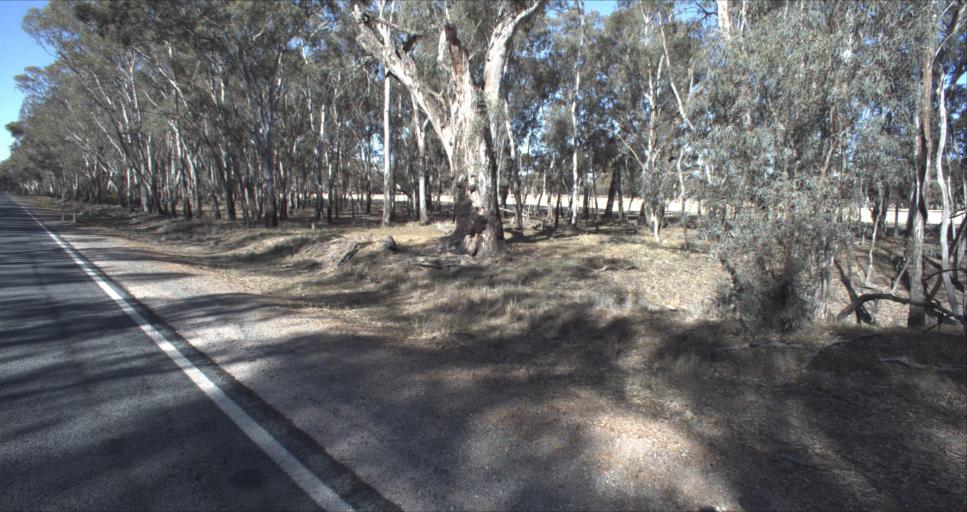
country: AU
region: New South Wales
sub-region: Leeton
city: Leeton
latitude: -34.6290
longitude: 146.3771
